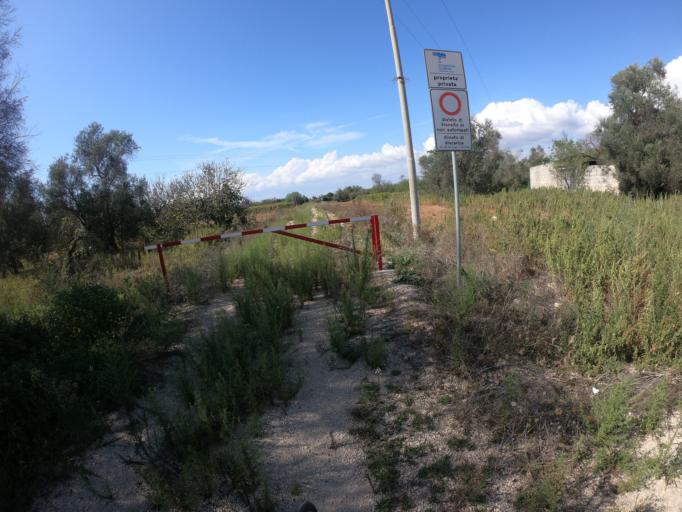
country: IT
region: Apulia
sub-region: Provincia di Lecce
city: Galatone
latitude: 40.1408
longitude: 18.0537
